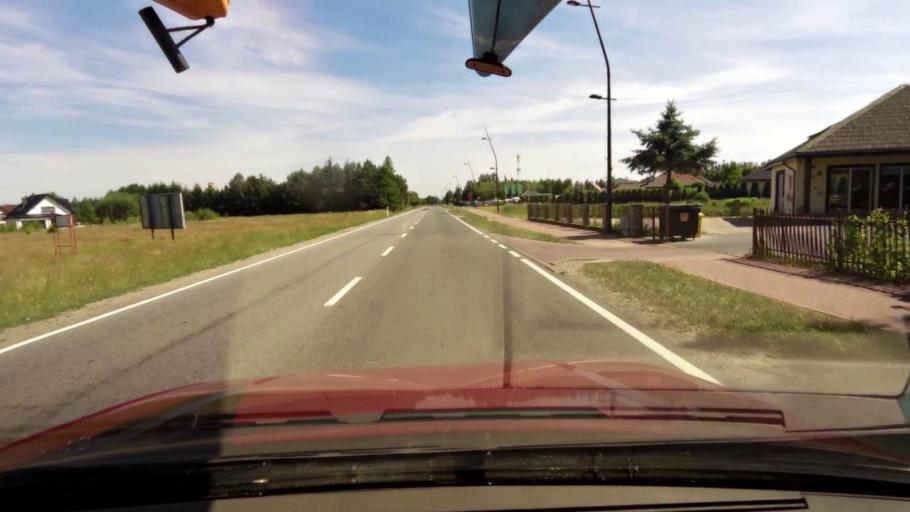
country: PL
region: Pomeranian Voivodeship
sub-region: Powiat slupski
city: Kobylnica
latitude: 54.4339
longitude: 17.0004
